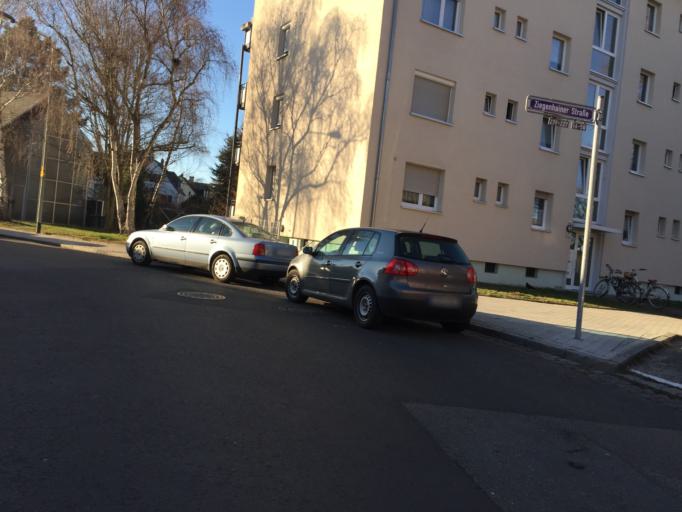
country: DE
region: Hesse
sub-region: Regierungsbezirk Darmstadt
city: Frankfurt am Main
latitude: 50.1553
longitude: 8.6706
